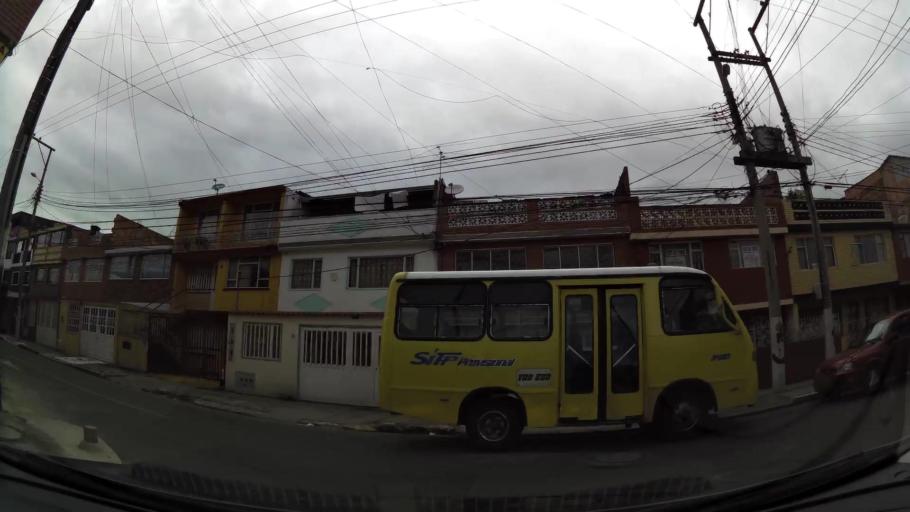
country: CO
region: Bogota D.C.
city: Bogota
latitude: 4.6916
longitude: -74.1048
